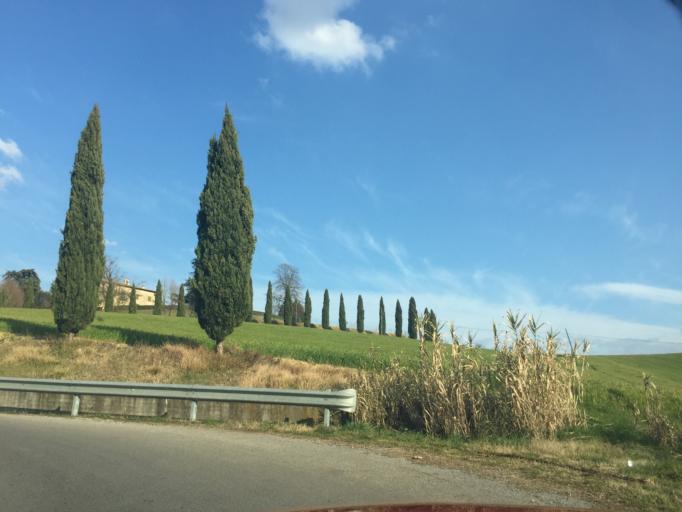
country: IT
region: Tuscany
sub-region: Province of Florence
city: Fucecchio
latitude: 43.7516
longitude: 10.8224
